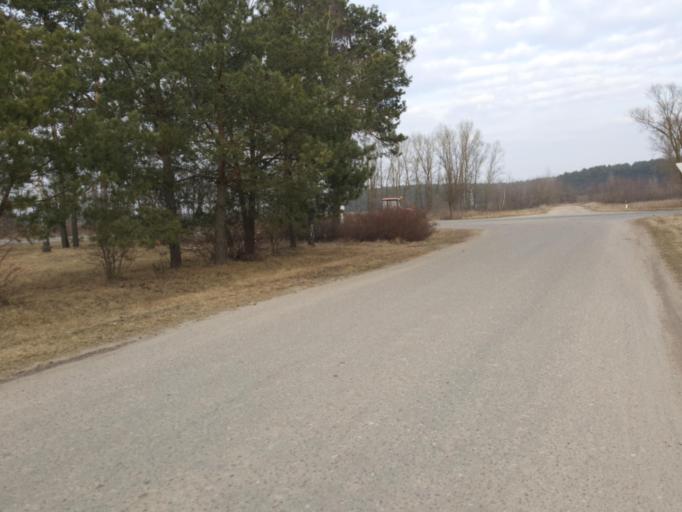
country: BY
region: Brest
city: Kamyanyets
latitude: 52.3346
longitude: 23.9110
